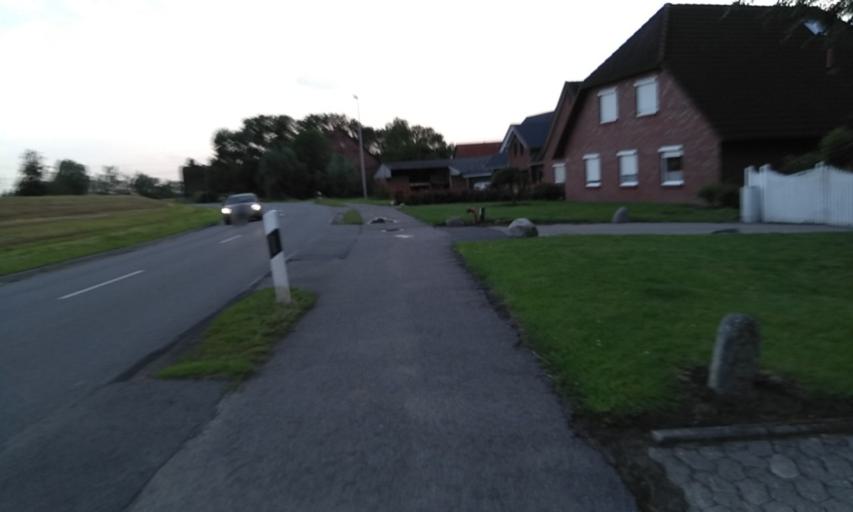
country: DE
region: Lower Saxony
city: Buxtehude
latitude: 53.4974
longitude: 9.7182
